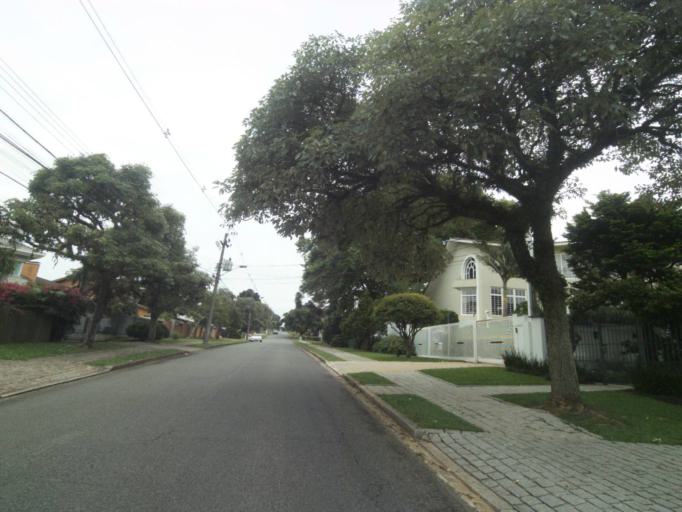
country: BR
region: Parana
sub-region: Curitiba
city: Curitiba
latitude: -25.4112
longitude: -49.2856
